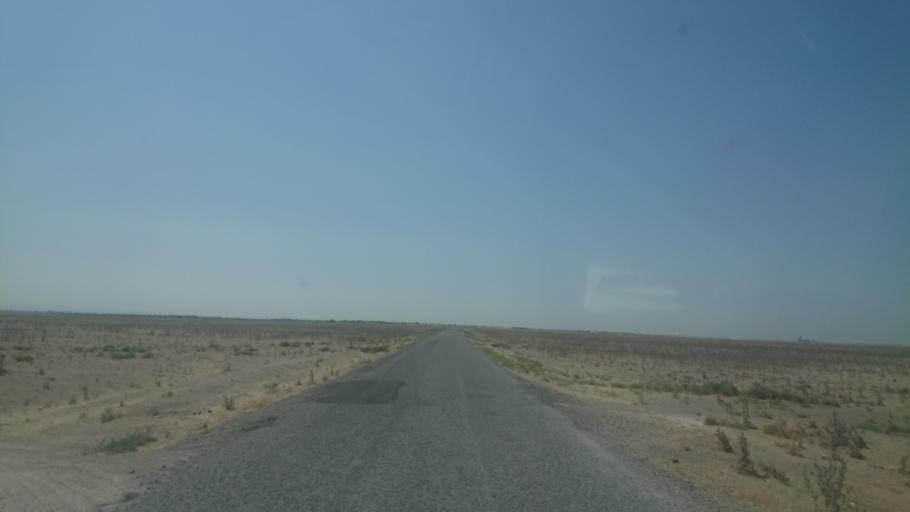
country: TR
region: Aksaray
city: Yesilova
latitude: 38.3115
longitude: 33.7378
